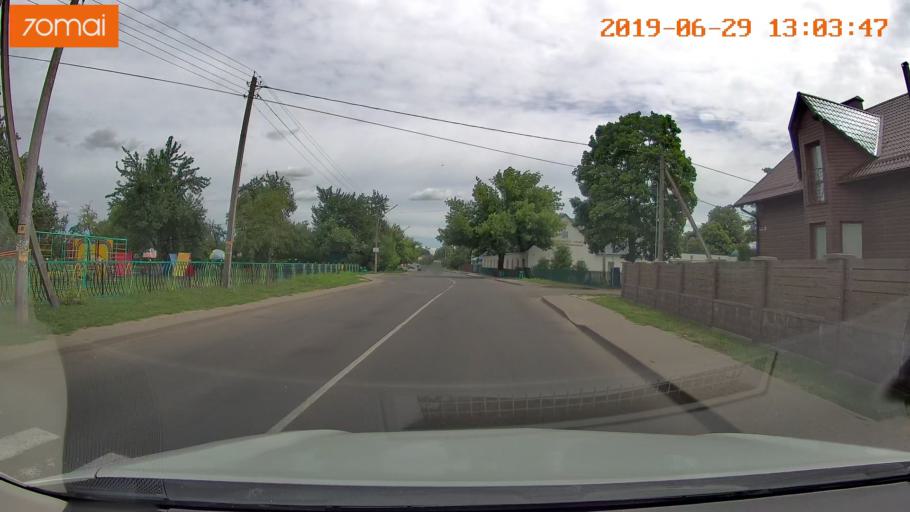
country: BY
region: Minsk
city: Slutsk
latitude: 53.0312
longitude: 27.5639
